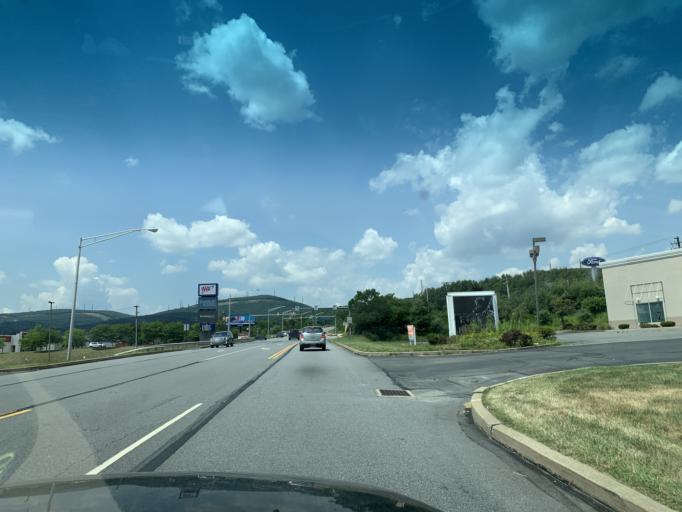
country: US
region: Pennsylvania
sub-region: Lackawanna County
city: Throop
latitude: 41.4551
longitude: -75.6470
